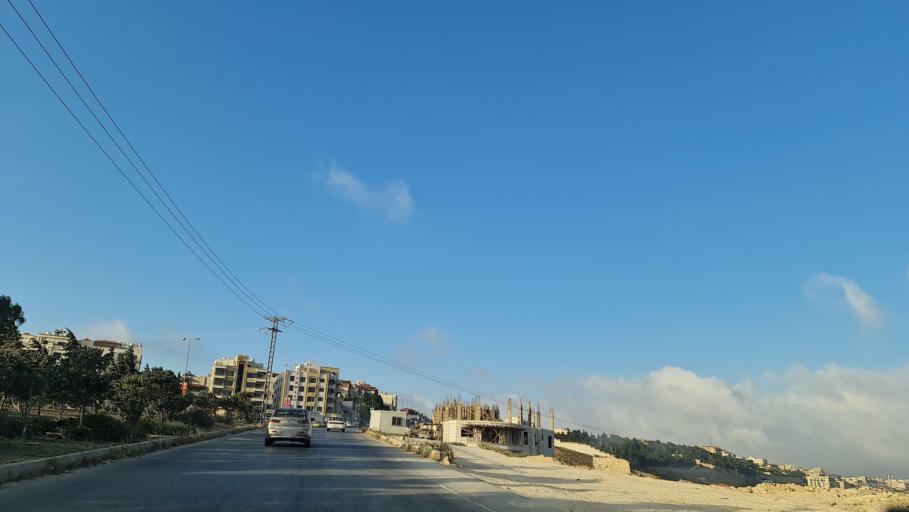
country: JO
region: Amman
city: Al Jubayhah
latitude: 32.0462
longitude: 35.8701
